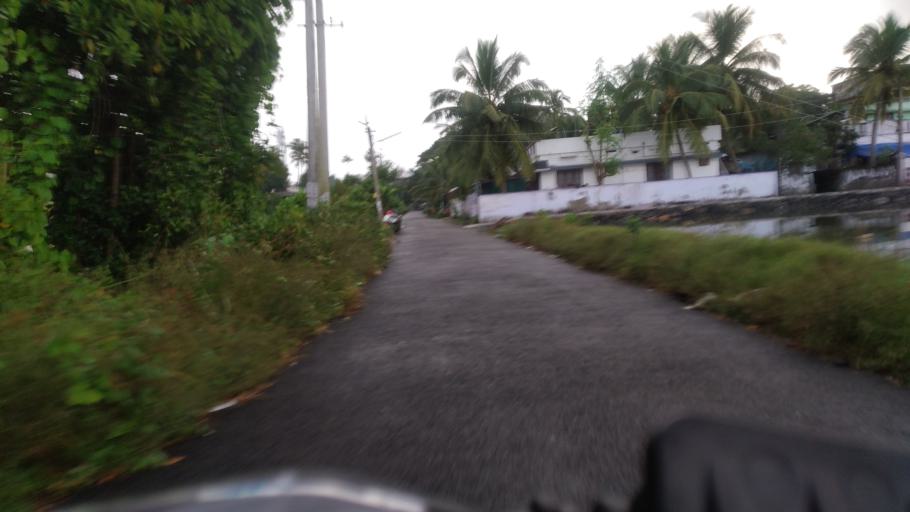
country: IN
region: Kerala
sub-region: Ernakulam
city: Elur
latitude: 10.0183
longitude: 76.2230
